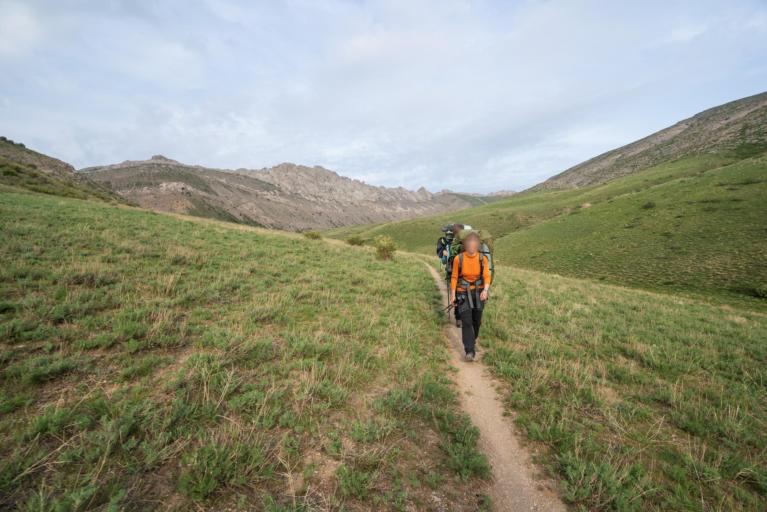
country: KZ
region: Ongtustik Qazaqstan
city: Ashchysay
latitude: 43.5797
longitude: 68.8916
